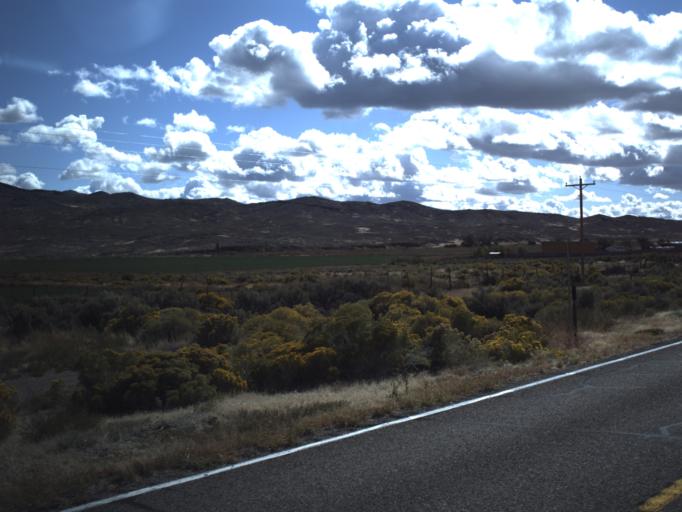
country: US
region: Nevada
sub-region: White Pine County
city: McGill
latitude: 38.9304
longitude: -114.0324
